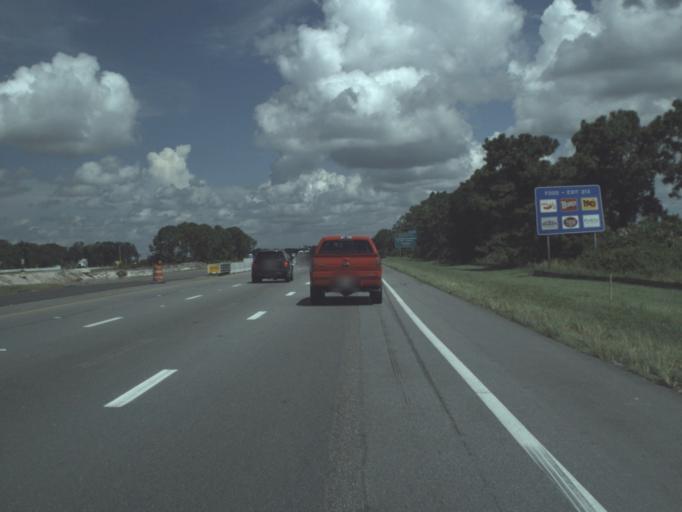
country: US
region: Florida
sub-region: Sarasota County
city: The Meadows
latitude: 27.3710
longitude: -82.4457
